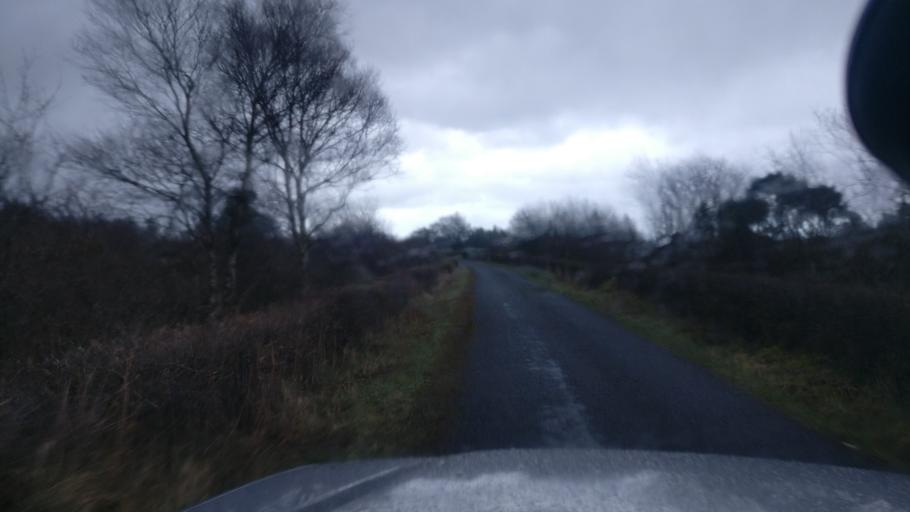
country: IE
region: Connaught
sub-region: County Galway
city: Loughrea
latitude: 53.2471
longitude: -8.4336
